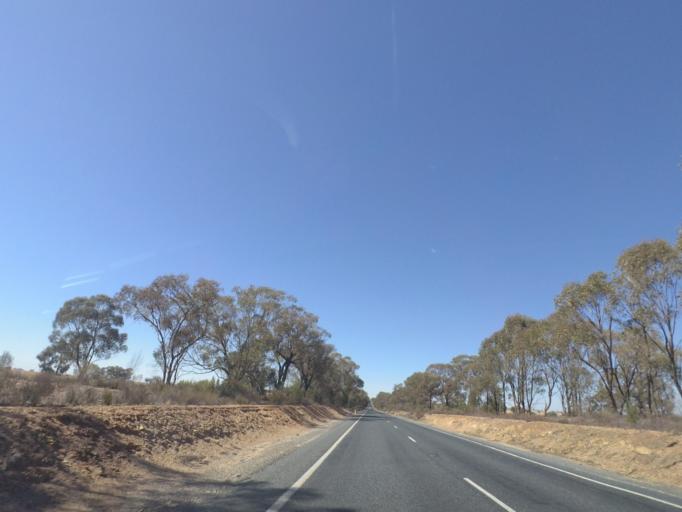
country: AU
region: New South Wales
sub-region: Bland
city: West Wyalong
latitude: -34.1445
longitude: 147.1196
